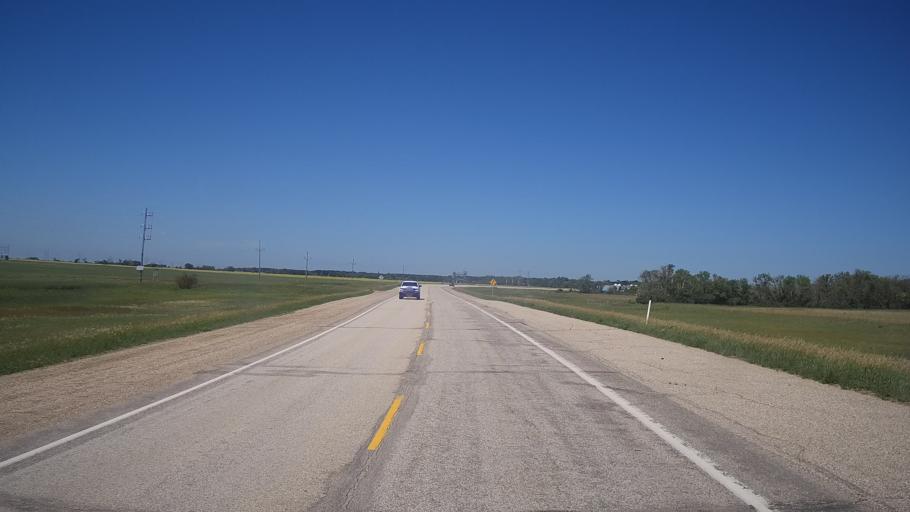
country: CA
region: Manitoba
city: Portage la Prairie
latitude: 50.1263
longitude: -98.5737
